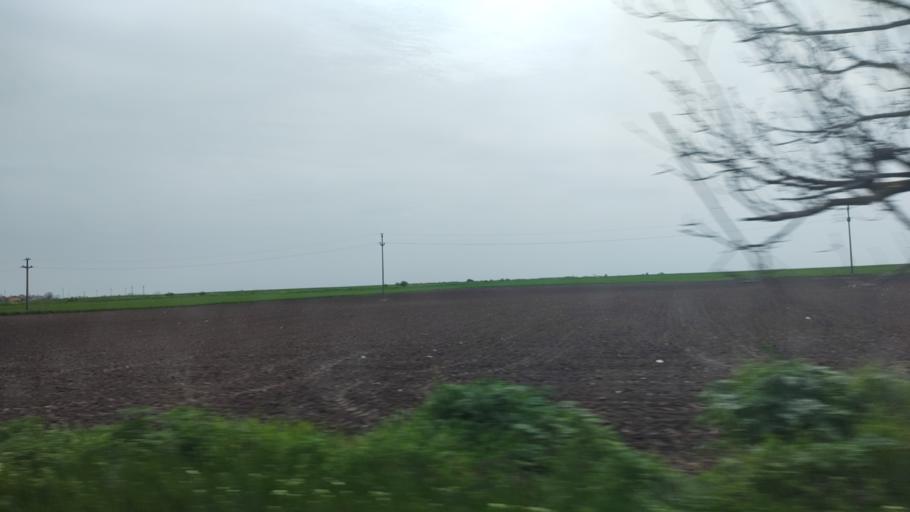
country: RO
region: Constanta
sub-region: Comuna Ciocarlia
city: Ciocarlia de Sus
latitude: 44.1143
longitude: 28.3181
